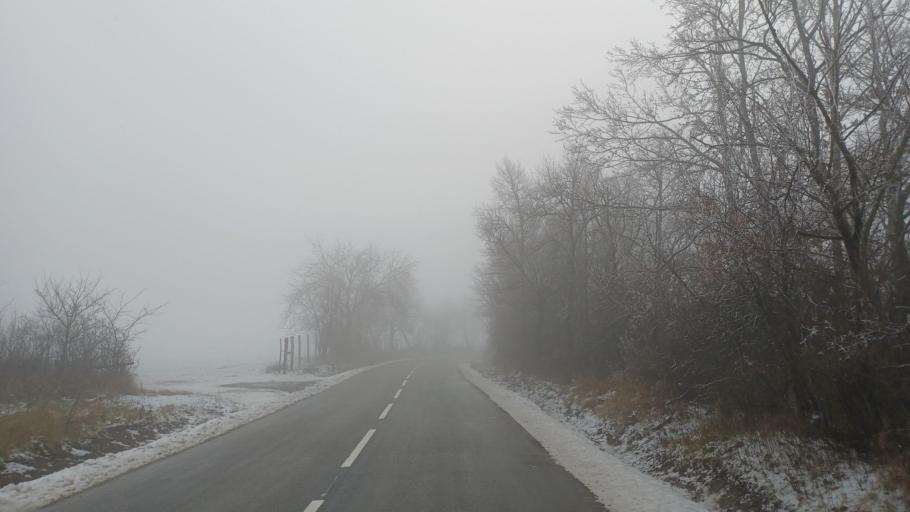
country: HU
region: Tolna
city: Gyonk
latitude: 46.5884
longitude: 18.4727
